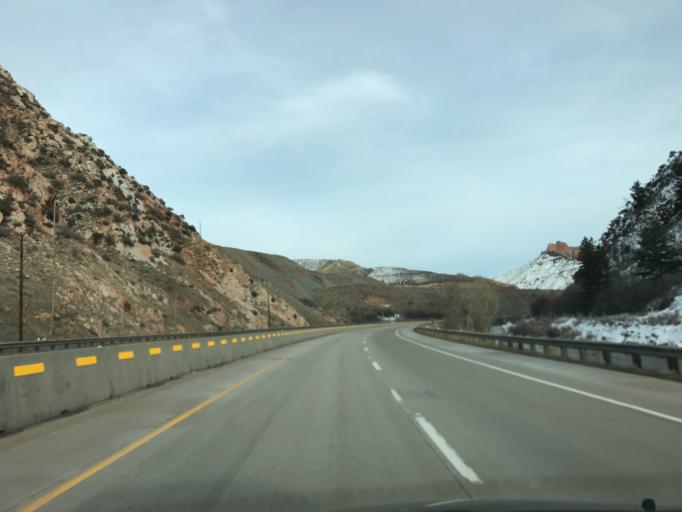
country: US
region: Utah
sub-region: Morgan County
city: Morgan
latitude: 41.0654
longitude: -111.5542
